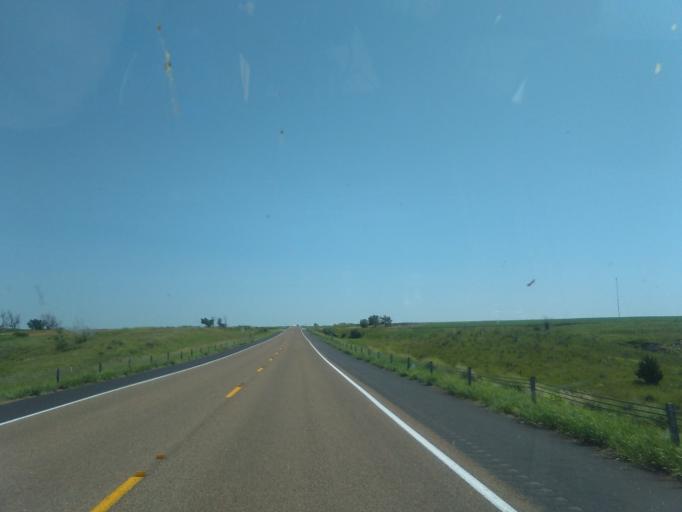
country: US
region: Nebraska
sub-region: Hitchcock County
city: Trenton
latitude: 40.2184
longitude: -100.9409
